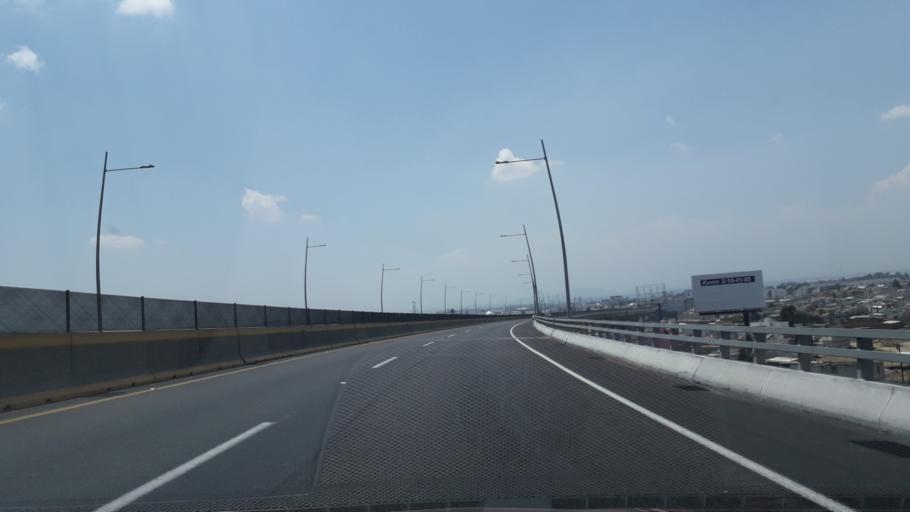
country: MX
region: Puebla
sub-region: Puebla
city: San Sebastian de Aparicio
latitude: 19.0818
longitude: -98.1694
